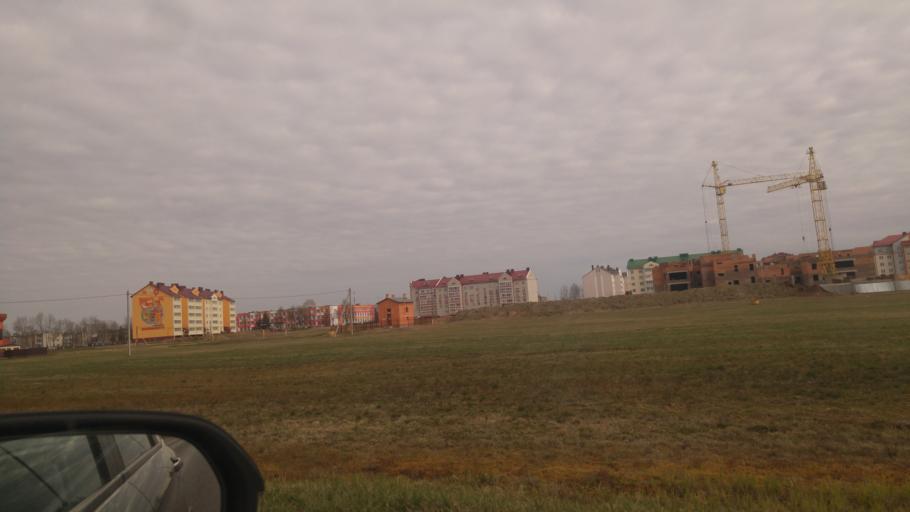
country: BY
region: Minsk
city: Chervyen'
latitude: 53.6988
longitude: 28.4208
